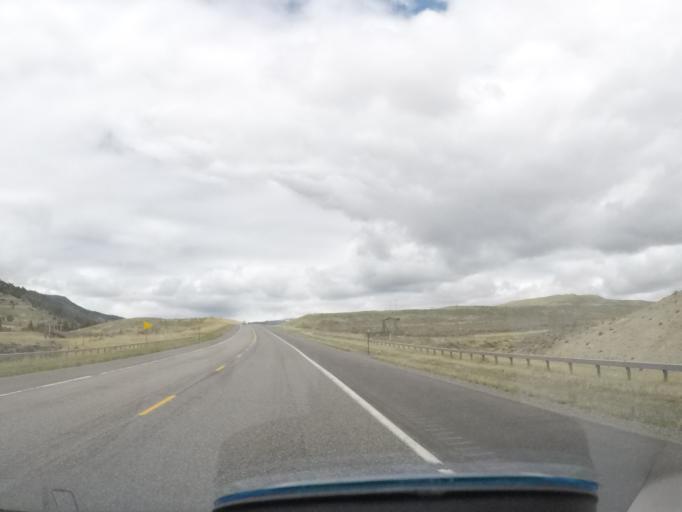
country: US
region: Wyoming
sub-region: Sublette County
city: Pinedale
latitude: 43.5833
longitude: -109.7662
